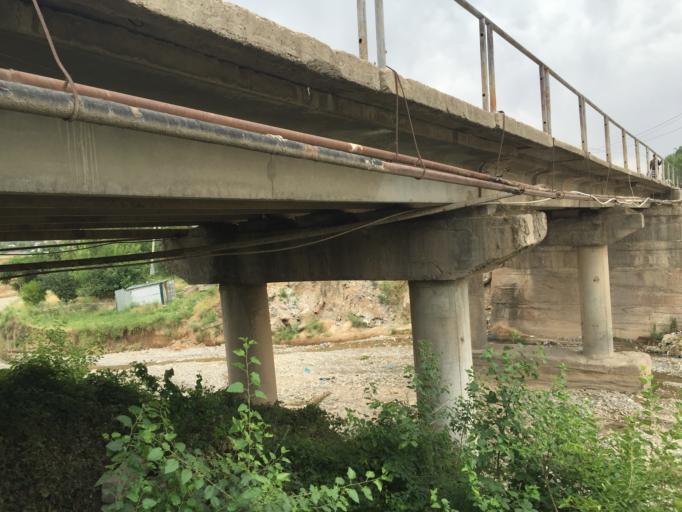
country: TJ
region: Khatlon
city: Kulob
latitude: 37.9135
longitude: 69.8170
